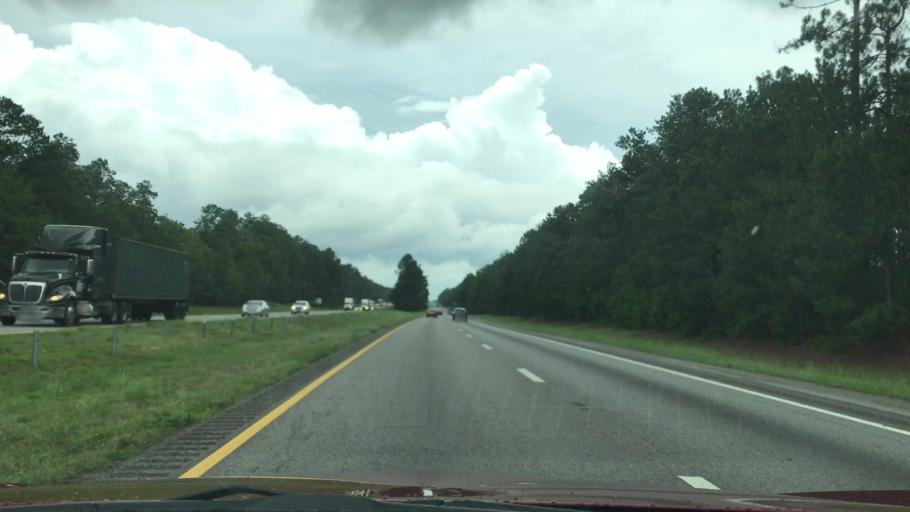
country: US
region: South Carolina
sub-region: Calhoun County
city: Saint Matthews
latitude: 33.6501
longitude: -80.8834
